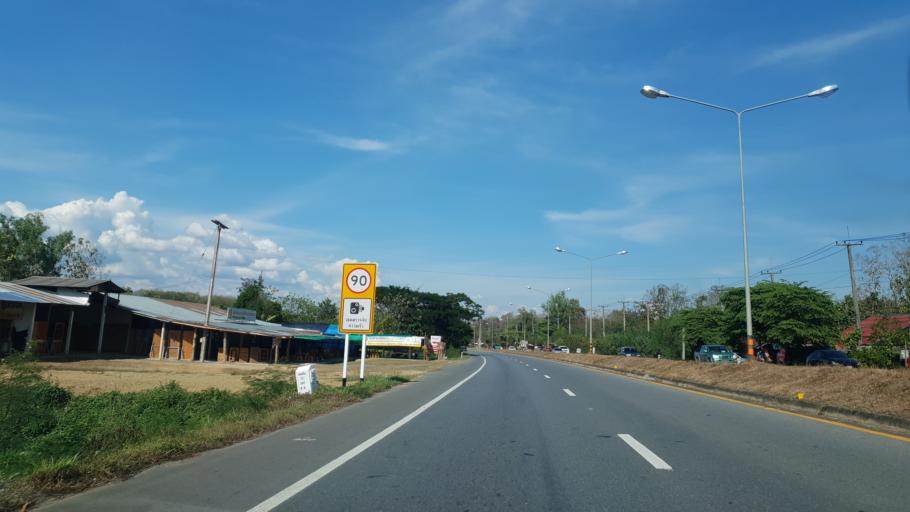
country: TH
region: Phrae
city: Den Chai
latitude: 17.9506
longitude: 100.0681
